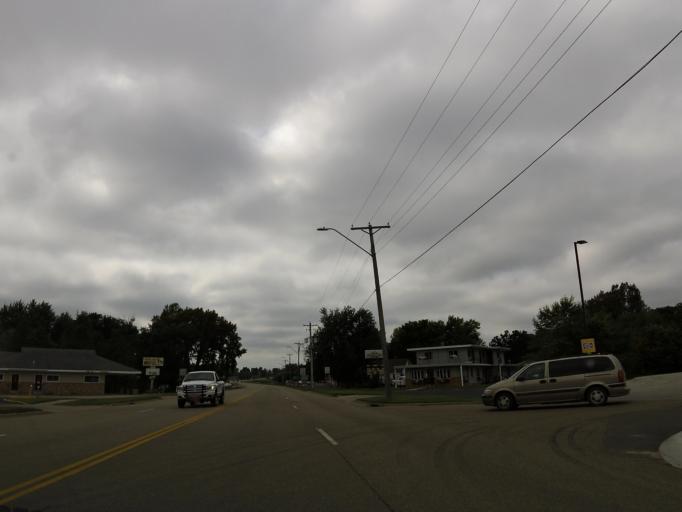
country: US
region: Minnesota
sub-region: Chippewa County
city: Montevideo
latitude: 44.9366
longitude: -95.7276
